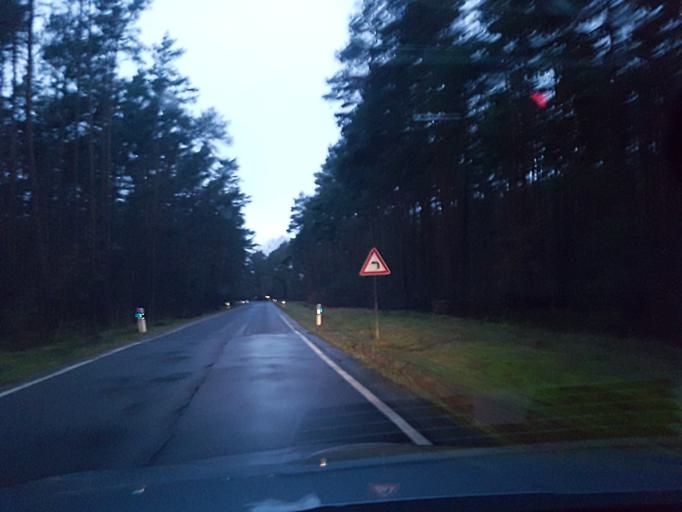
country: DE
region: Brandenburg
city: Bad Liebenwerda
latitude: 51.5463
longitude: 13.4317
